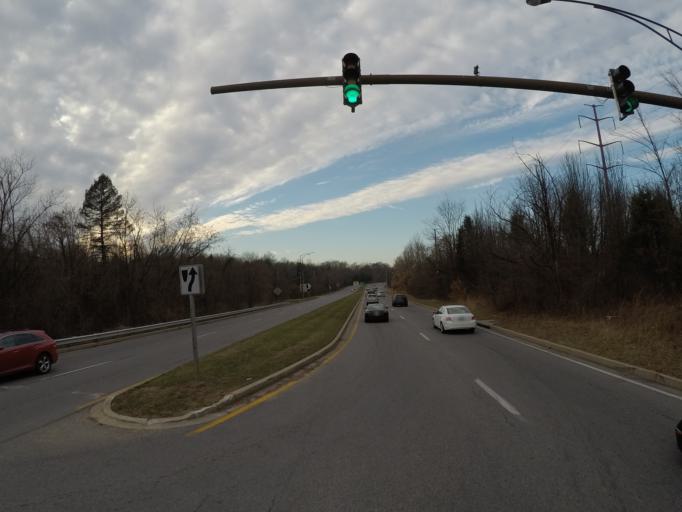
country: US
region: Maryland
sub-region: Howard County
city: Riverside
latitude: 39.2032
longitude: -76.8614
